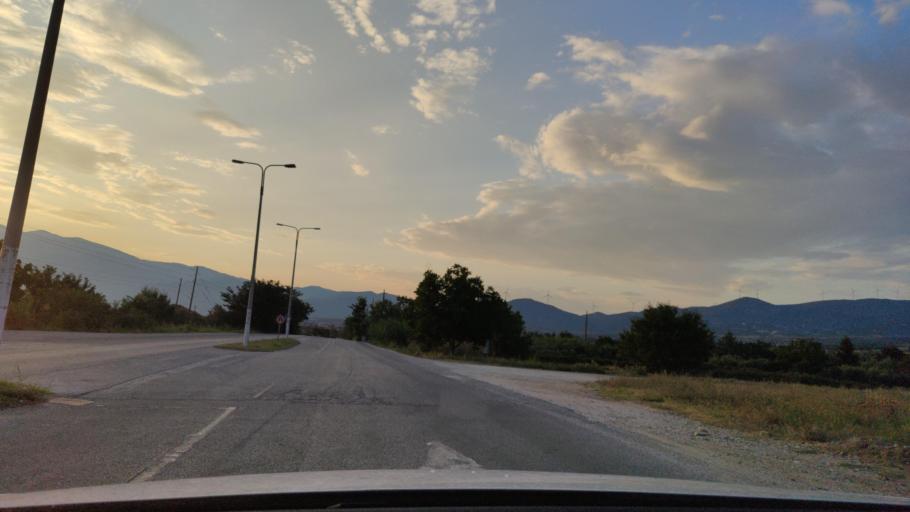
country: GR
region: Central Macedonia
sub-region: Nomos Serron
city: Charopo
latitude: 41.2471
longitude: 23.3787
